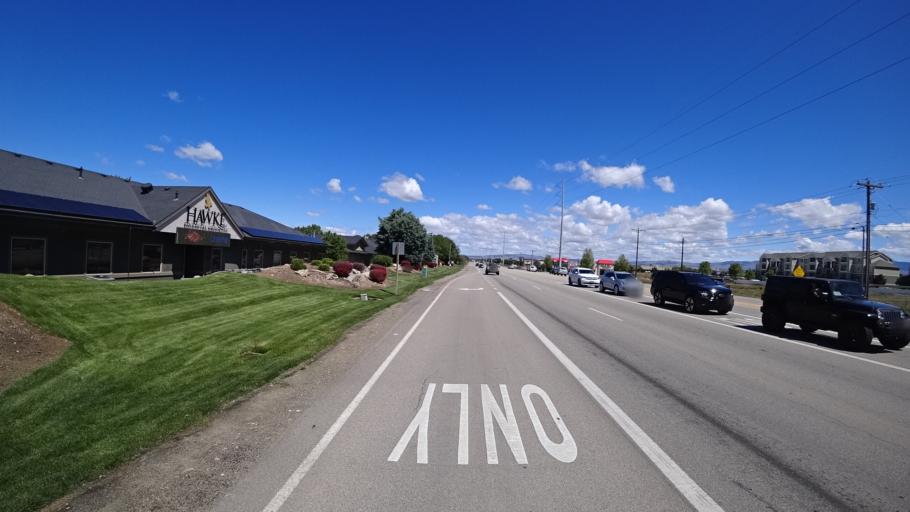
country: US
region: Idaho
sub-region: Ada County
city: Meridian
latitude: 43.6270
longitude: -116.3547
